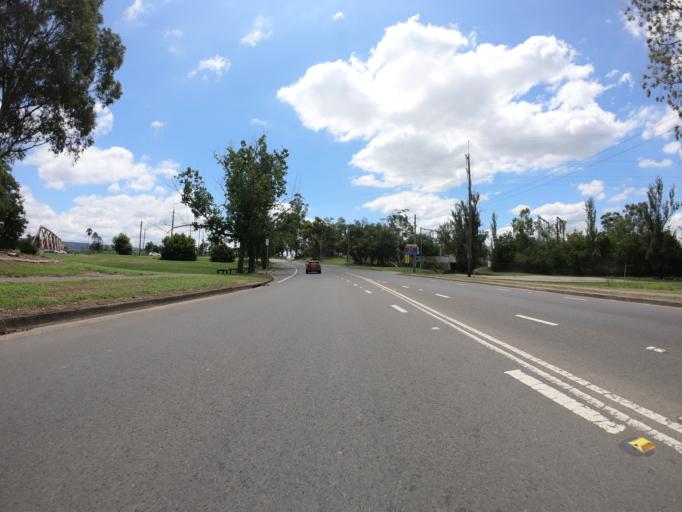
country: AU
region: New South Wales
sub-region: Penrith Municipality
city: Penrith
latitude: -33.7479
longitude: 150.6841
